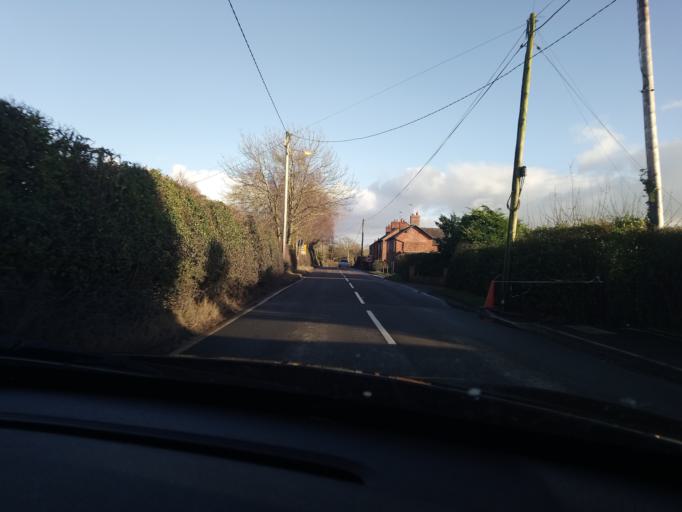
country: GB
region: Wales
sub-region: Wrexham
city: Overton
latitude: 52.9219
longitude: -2.9294
